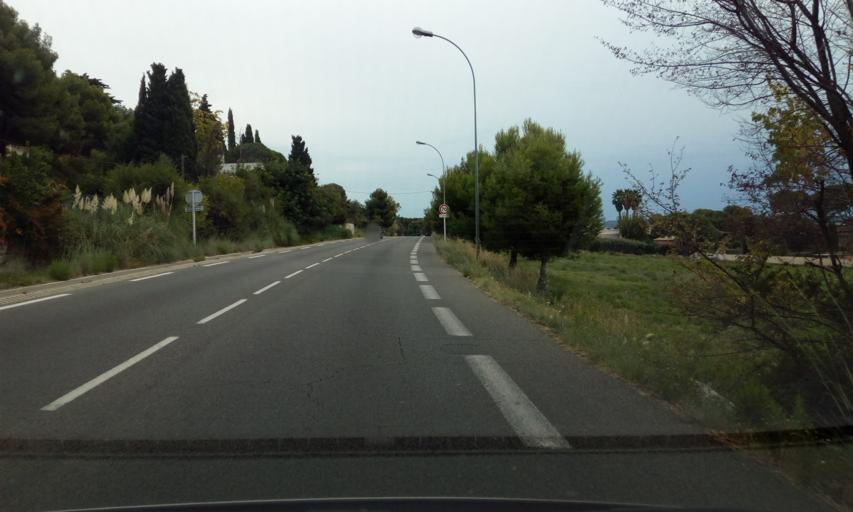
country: FR
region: Provence-Alpes-Cote d'Azur
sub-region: Departement du Var
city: Carqueiranne
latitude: 43.0882
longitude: 6.0920
